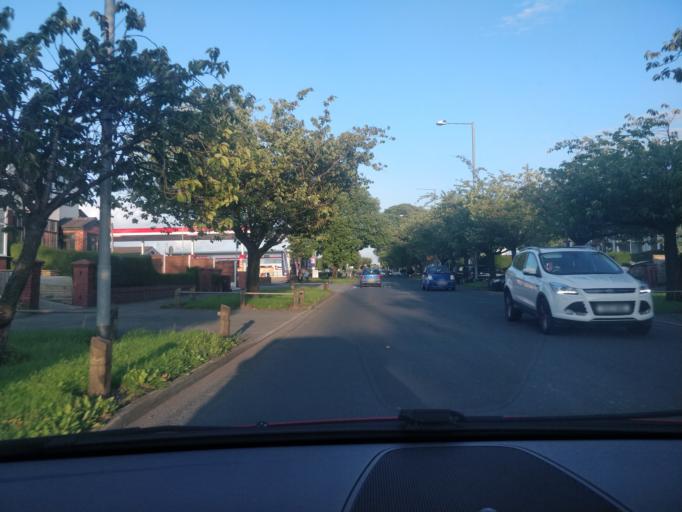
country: GB
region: England
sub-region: Lancashire
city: Preston
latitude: 53.7731
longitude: -2.6826
